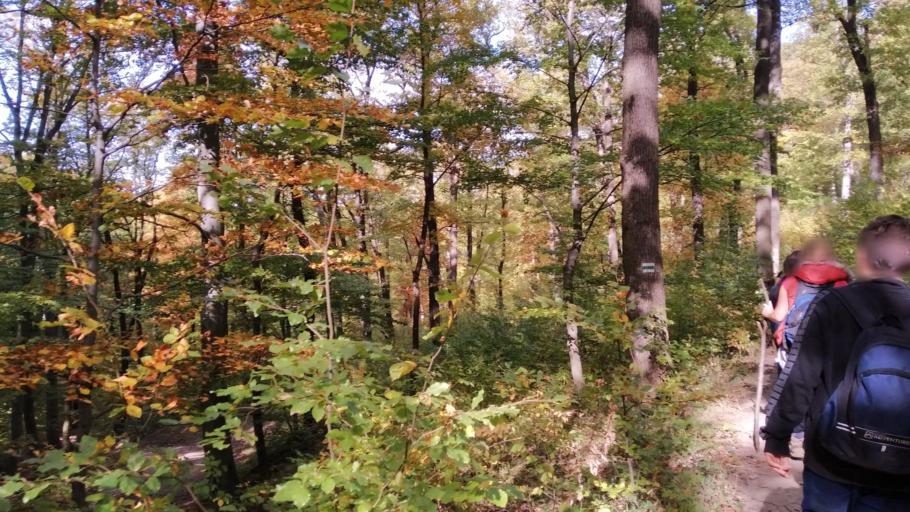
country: HU
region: Pest
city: Visegrad
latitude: 47.7404
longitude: 18.9672
